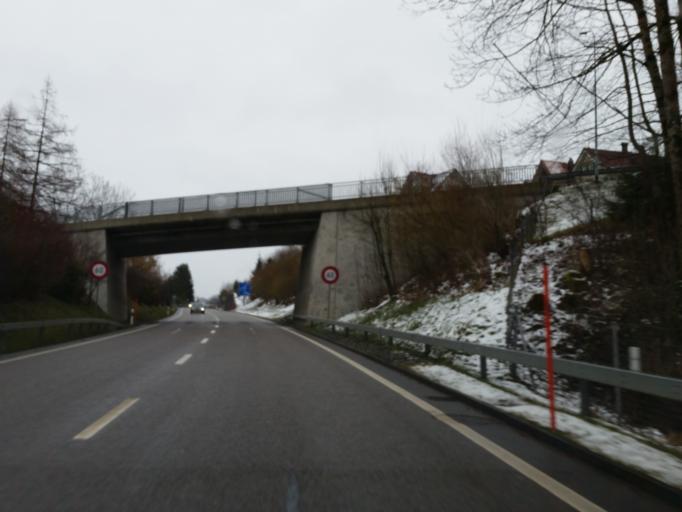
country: CH
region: Appenzell Ausserrhoden
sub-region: Bezirk Mittelland
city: Teufen
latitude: 47.3860
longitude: 9.3857
